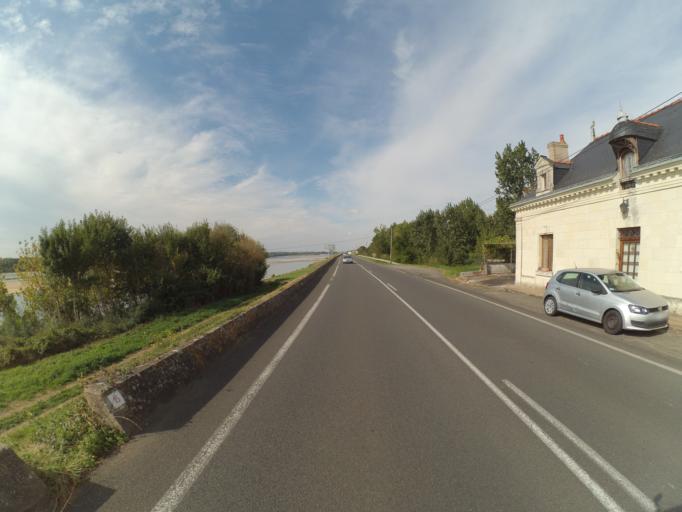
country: FR
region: Pays de la Loire
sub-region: Departement de Maine-et-Loire
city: Varennes-sur-Loire
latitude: 47.2280
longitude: 0.0491
